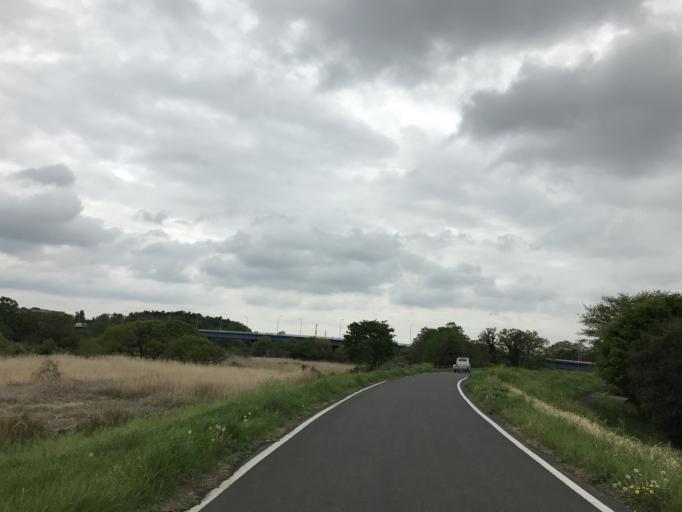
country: JP
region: Ibaraki
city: Mitsukaido
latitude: 36.0418
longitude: 140.0248
